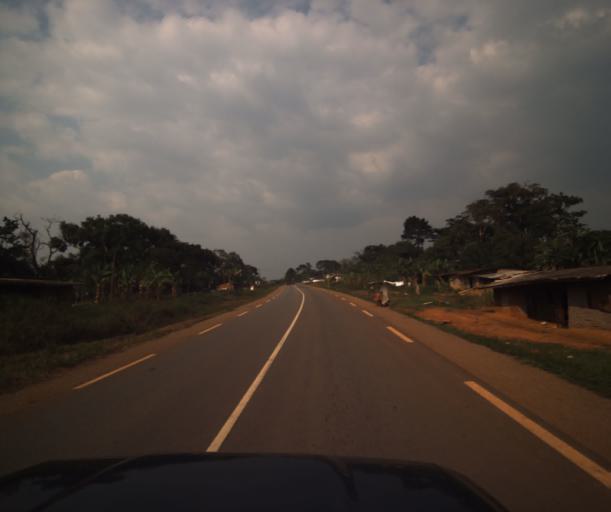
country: CM
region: Centre
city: Mbankomo
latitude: 3.7065
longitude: 11.3775
